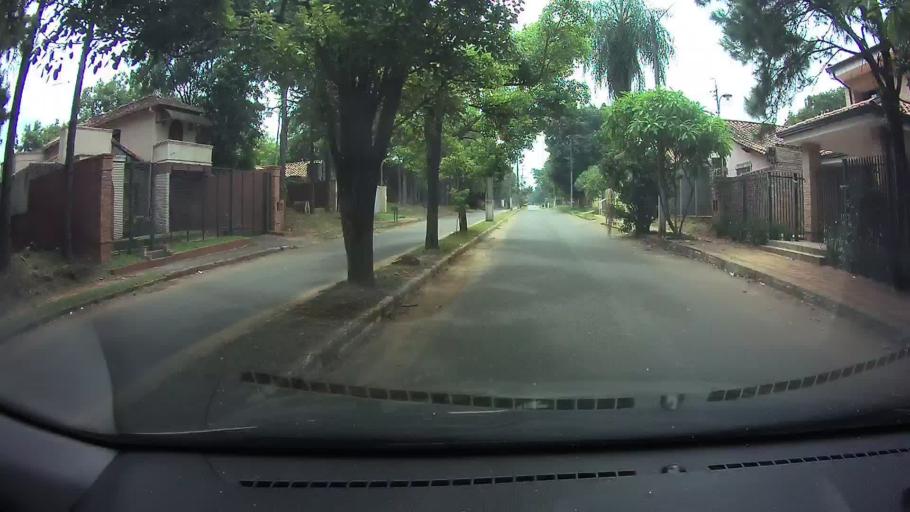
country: PY
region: Central
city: San Lorenzo
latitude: -25.2912
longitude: -57.5090
